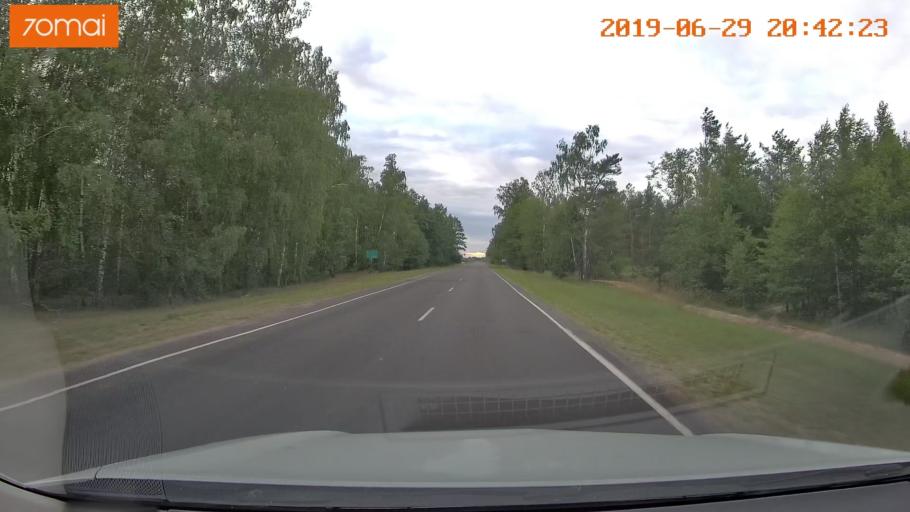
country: BY
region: Brest
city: Hantsavichy
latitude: 52.5969
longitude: 26.3268
